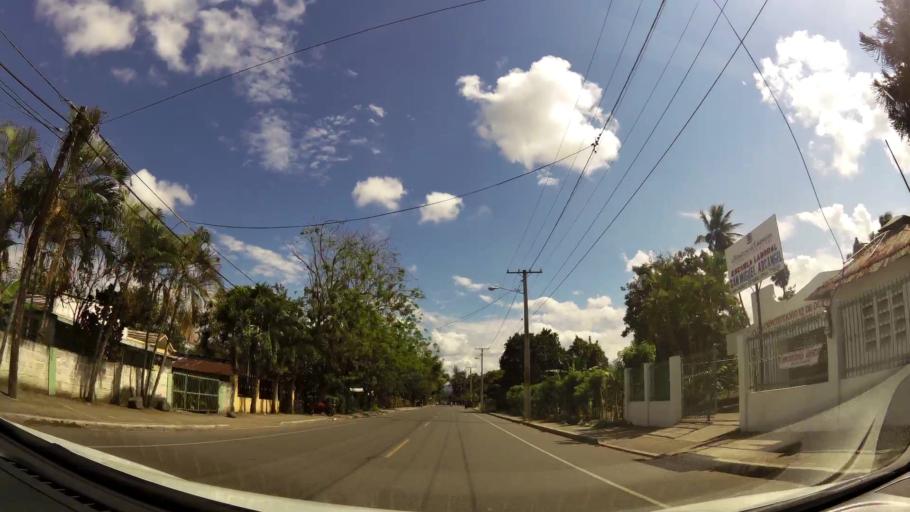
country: DO
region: La Vega
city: Concepcion de La Vega
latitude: 19.2437
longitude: -70.5374
